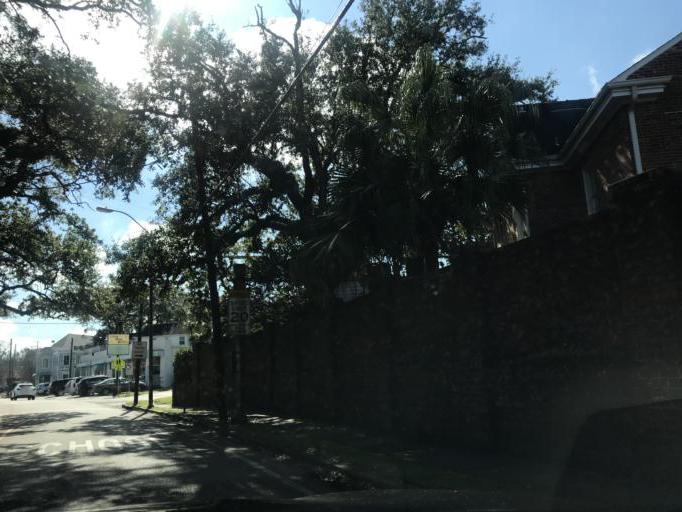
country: US
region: Louisiana
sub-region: Jefferson Parish
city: Metairie
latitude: 29.9817
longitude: -90.1278
